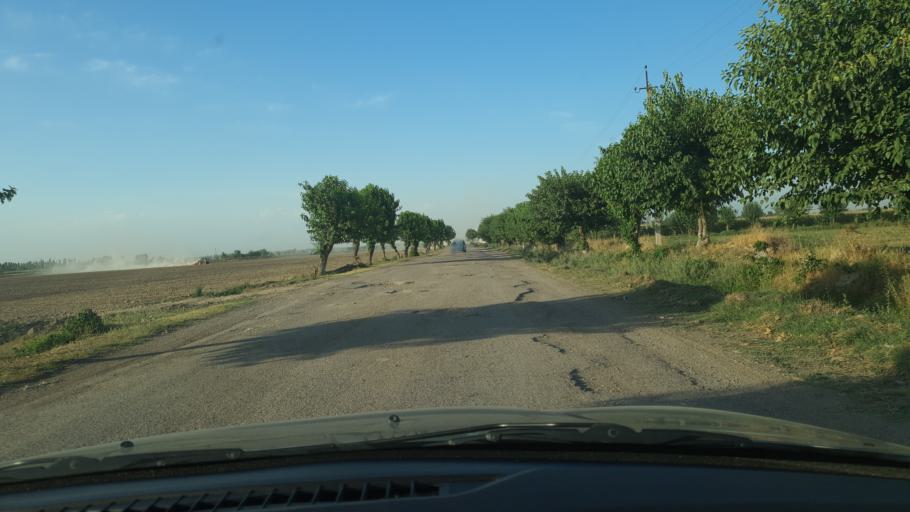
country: UZ
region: Toshkent
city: Tuytepa
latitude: 41.0954
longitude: 69.3730
